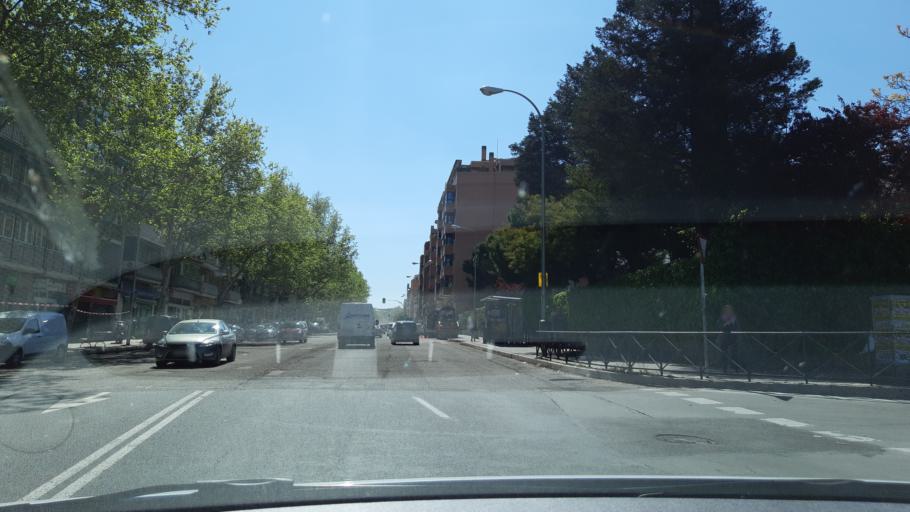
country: ES
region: Madrid
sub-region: Provincia de Madrid
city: San Blas
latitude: 40.4486
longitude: -3.6092
